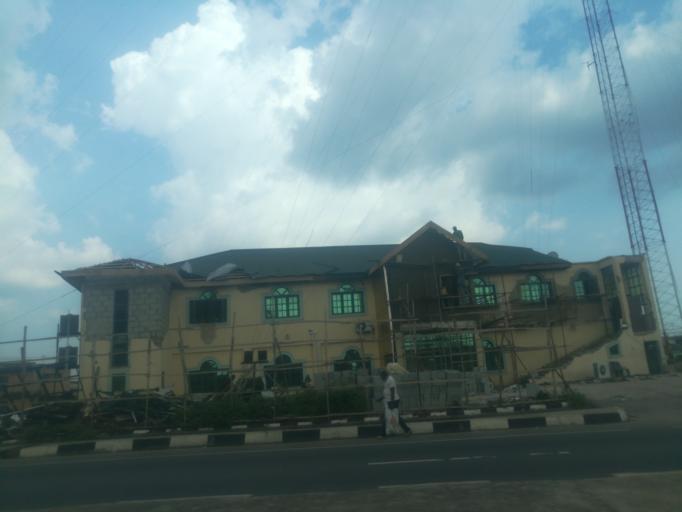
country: NG
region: Oyo
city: Ibadan
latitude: 7.3379
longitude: 3.8772
